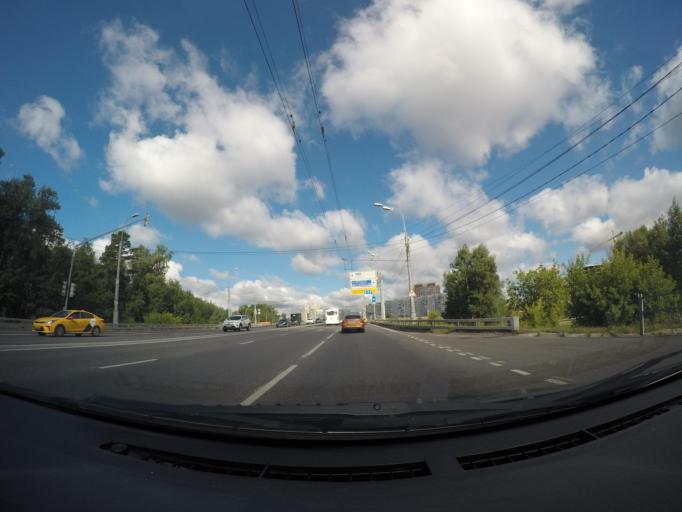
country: RU
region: Moscow
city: Khimki
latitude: 55.8755
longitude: 37.4322
